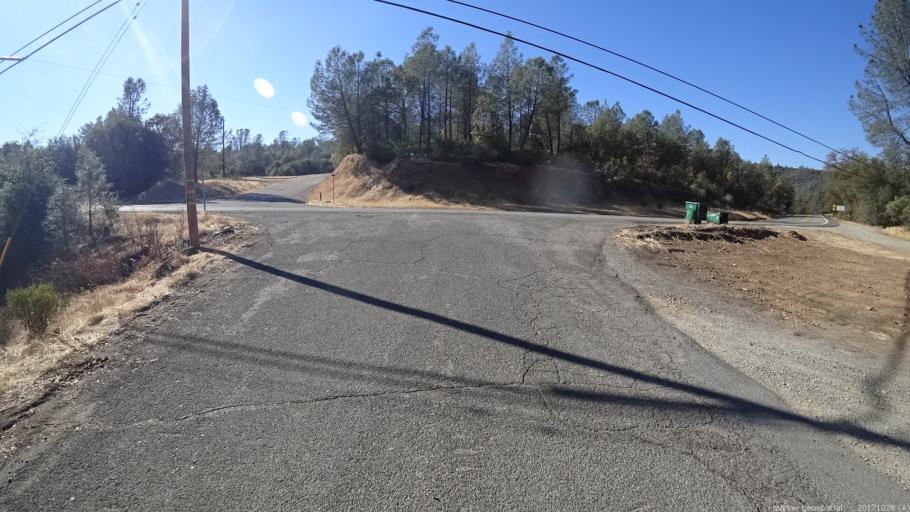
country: US
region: California
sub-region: Shasta County
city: Shasta
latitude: 40.5909
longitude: -122.4606
